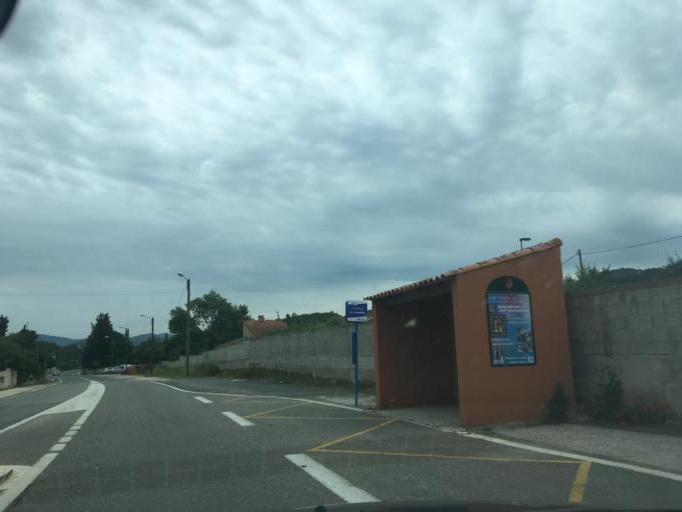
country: FR
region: Provence-Alpes-Cote d'Azur
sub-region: Departement du Var
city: Pierrefeu-du-Var
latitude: 43.2324
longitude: 6.1569
